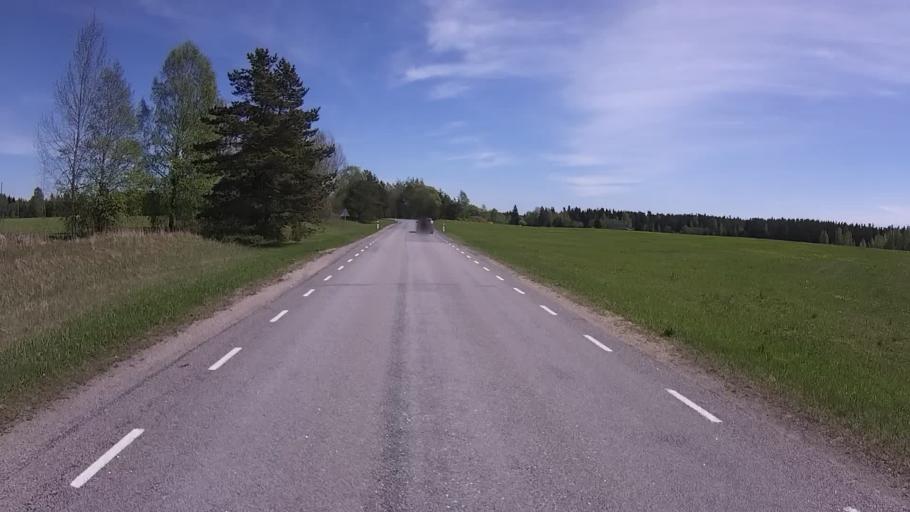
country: EE
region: Vorumaa
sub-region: Antsla vald
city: Vana-Antsla
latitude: 57.6137
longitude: 26.3687
